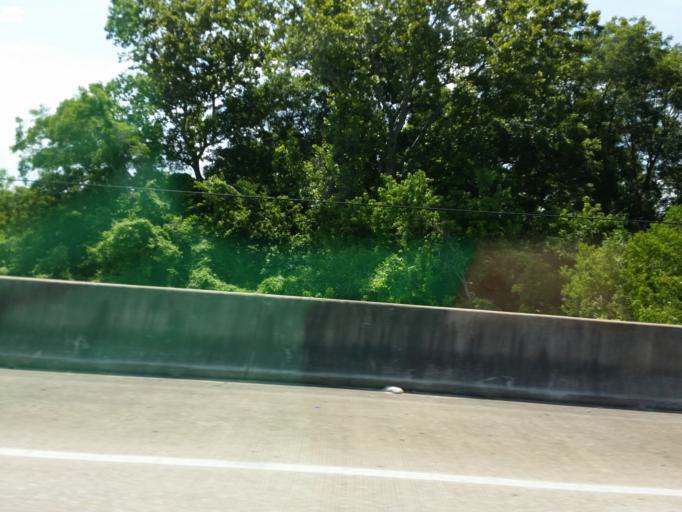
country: US
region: Alabama
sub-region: Marengo County
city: Demopolis
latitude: 32.5260
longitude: -87.8375
